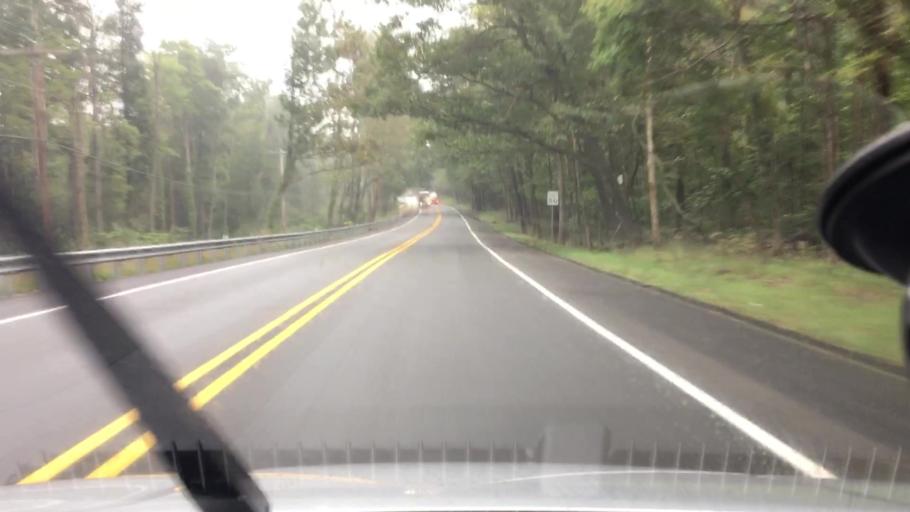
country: US
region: Pennsylvania
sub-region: Monroe County
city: Mount Pocono
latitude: 41.1290
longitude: -75.3275
